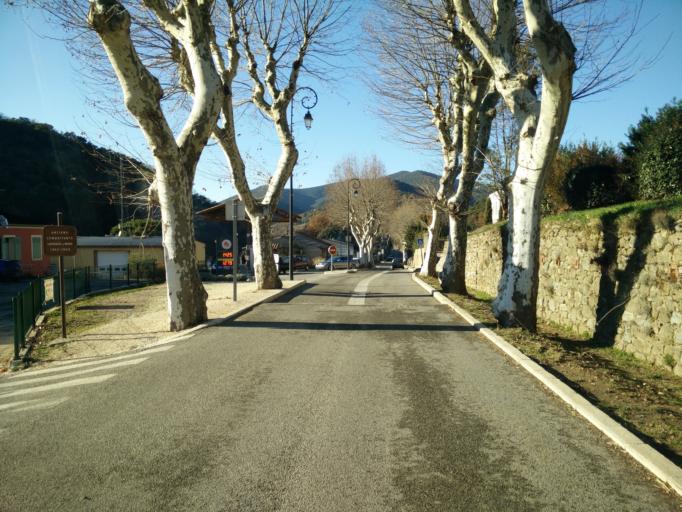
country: FR
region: Provence-Alpes-Cote d'Azur
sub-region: Departement du Var
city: Collobrieres
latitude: 43.2372
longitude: 6.3042
